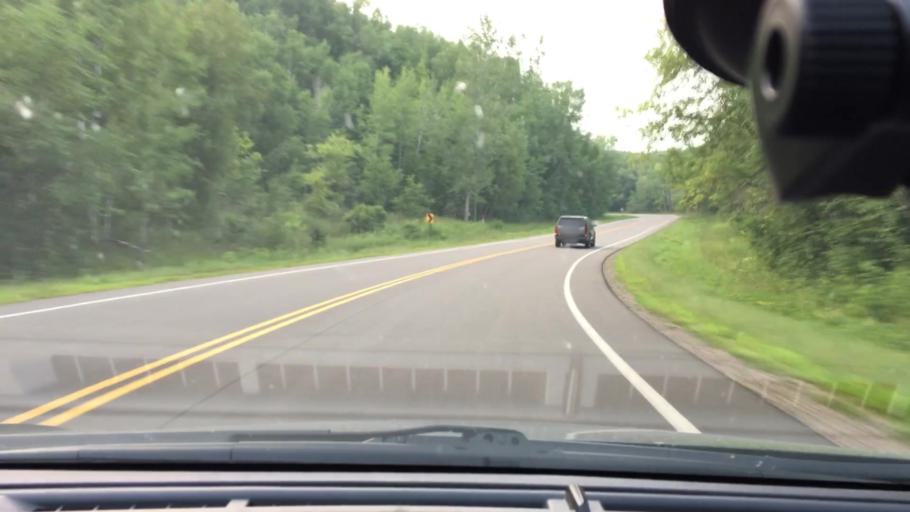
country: US
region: Minnesota
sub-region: Crow Wing County
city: Crosby
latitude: 46.5205
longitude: -93.9244
